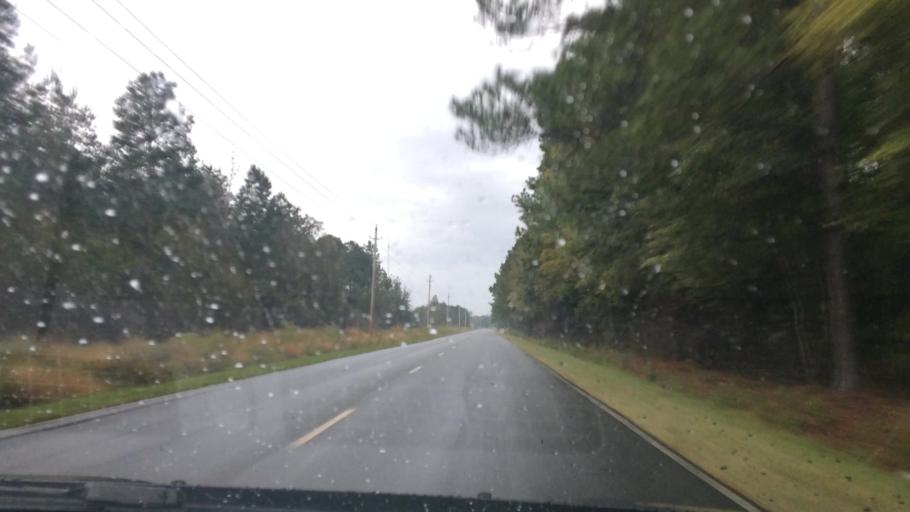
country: US
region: North Carolina
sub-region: Pitt County
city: Grifton
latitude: 35.3988
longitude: -77.4044
